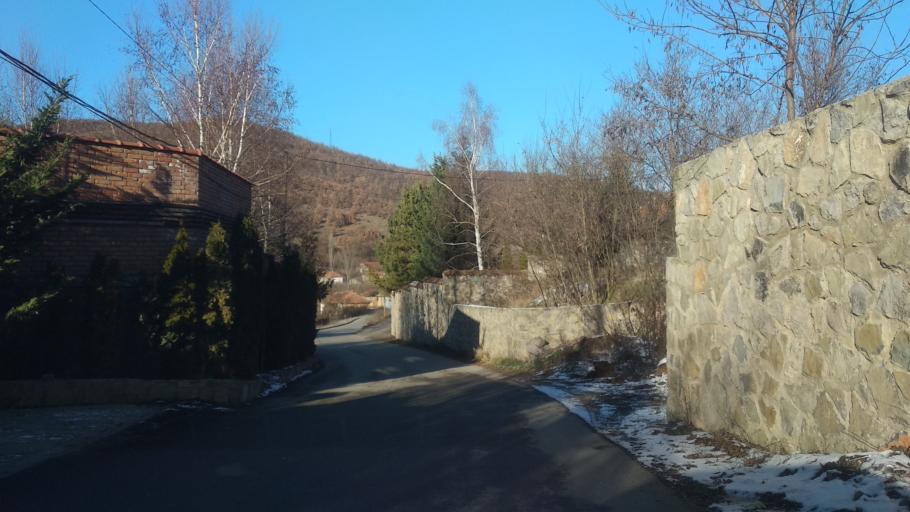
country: XK
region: Pristina
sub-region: Komuna e Prishtines
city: Pristina
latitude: 42.7130
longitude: 21.1690
